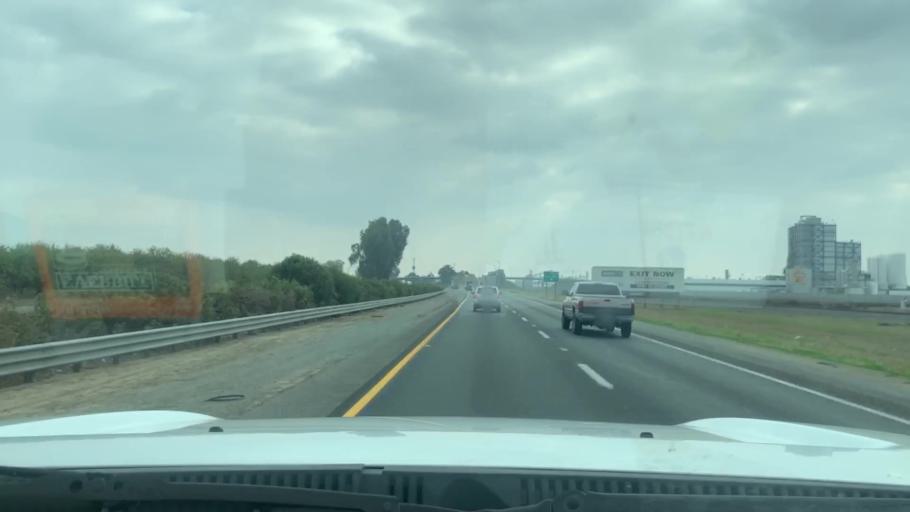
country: US
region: California
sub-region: Tulare County
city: Pixley
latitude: 36.0135
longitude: -119.3036
